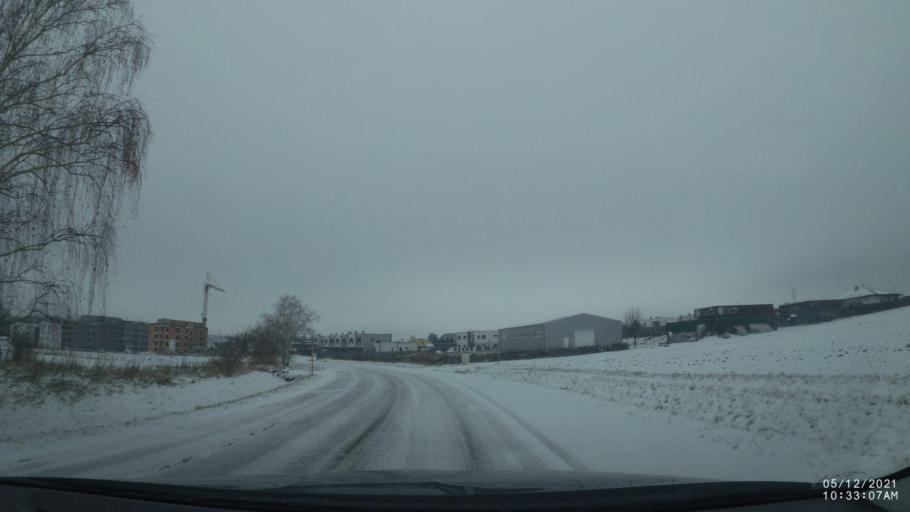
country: CZ
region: Kralovehradecky
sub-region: Okres Rychnov nad Kneznou
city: Rychnov nad Kneznou
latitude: 50.1637
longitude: 16.2920
